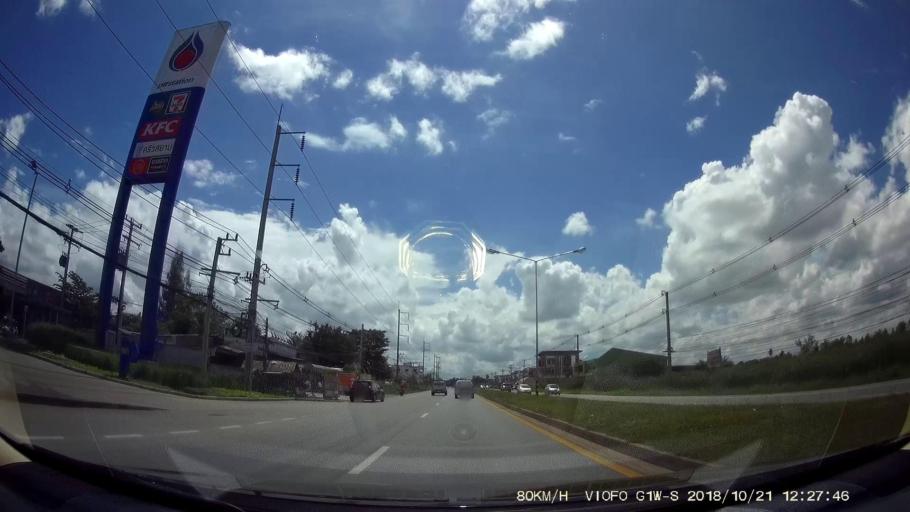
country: TH
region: Nakhon Ratchasima
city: Dan Khun Thot
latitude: 15.1976
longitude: 101.7630
